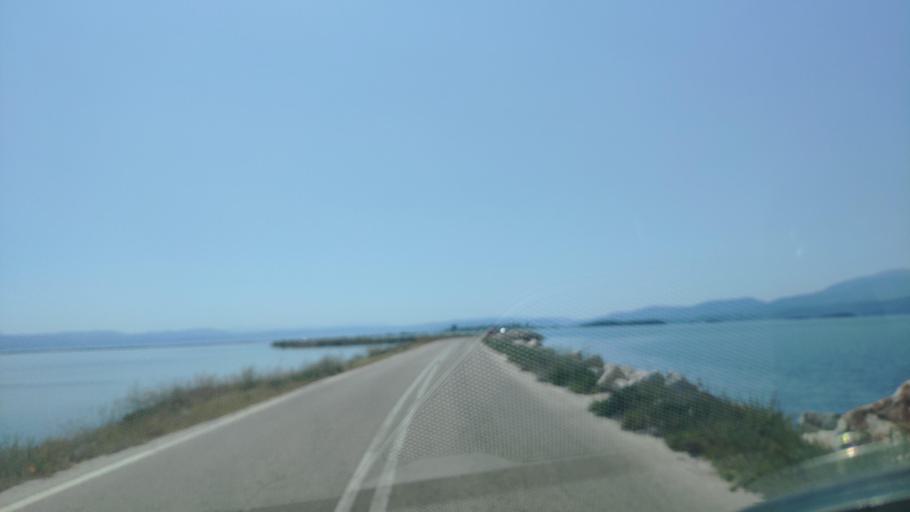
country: GR
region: Epirus
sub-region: Nomos Artas
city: Aneza
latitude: 39.0334
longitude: 20.8924
